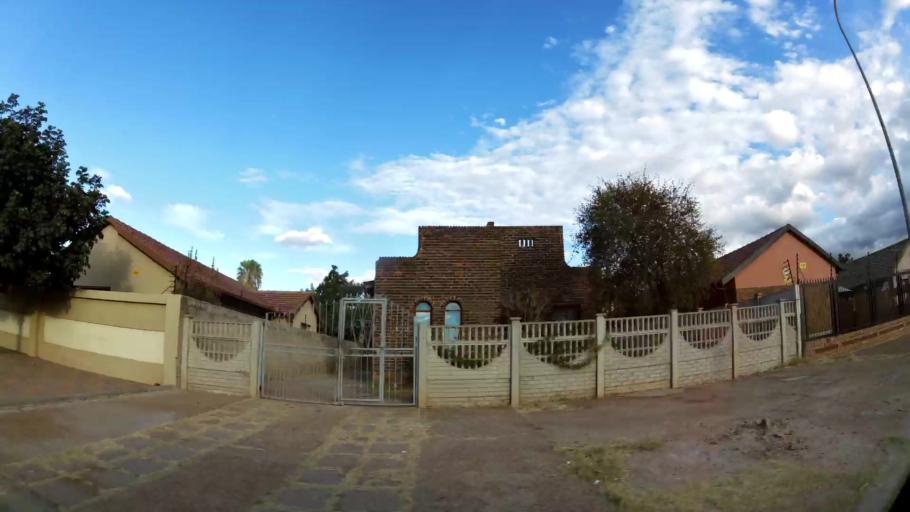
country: ZA
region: Limpopo
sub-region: Capricorn District Municipality
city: Polokwane
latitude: -23.9046
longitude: 29.4274
